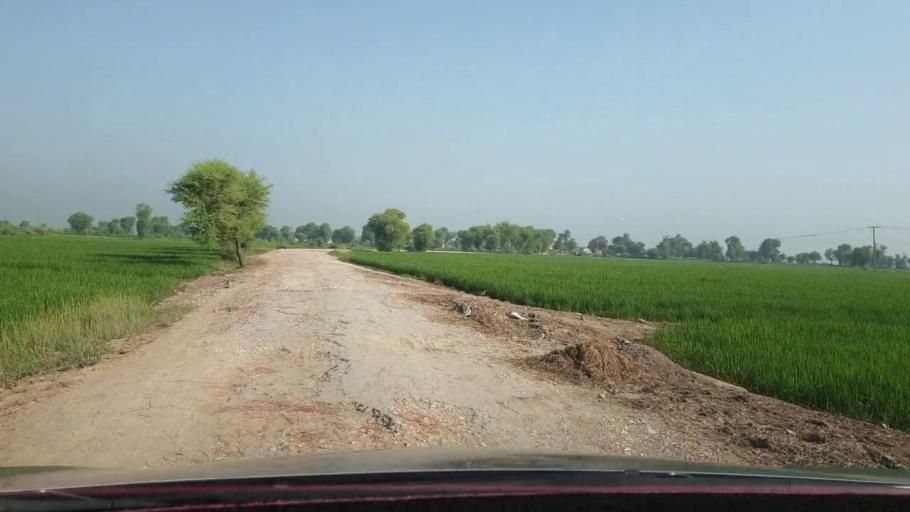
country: PK
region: Sindh
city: Nasirabad
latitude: 27.4457
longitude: 67.9192
